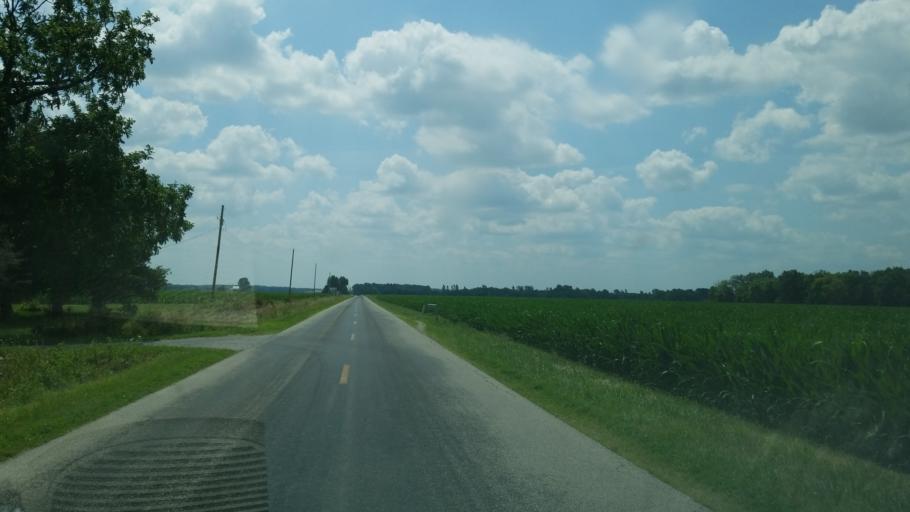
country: US
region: Ohio
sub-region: Henry County
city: Napoleon
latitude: 41.3505
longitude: -84.1346
